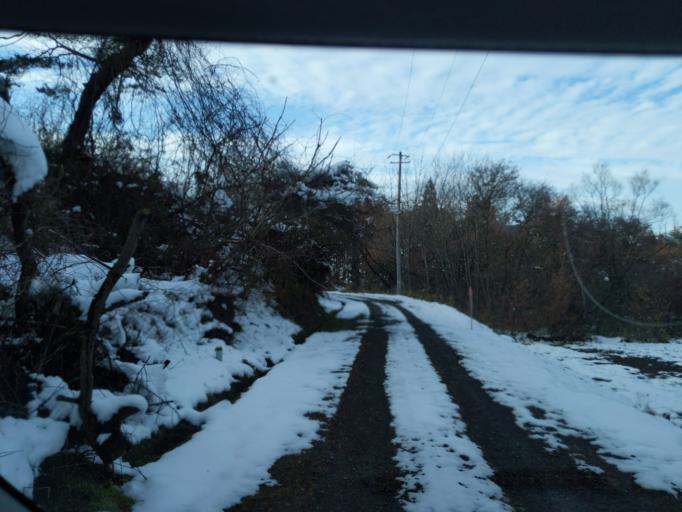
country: JP
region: Iwate
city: Mizusawa
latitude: 39.0377
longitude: 141.1038
